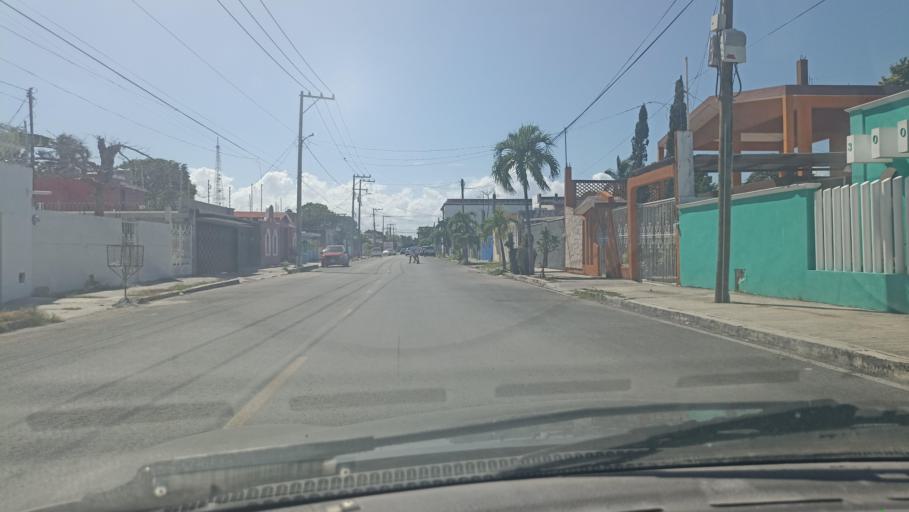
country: MX
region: Quintana Roo
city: Chetumal
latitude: 18.5101
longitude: -88.2905
